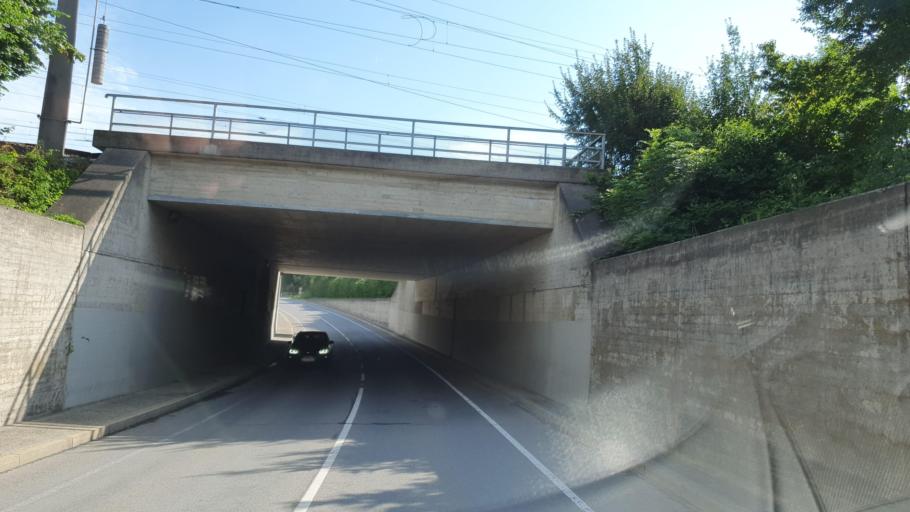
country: AT
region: Vorarlberg
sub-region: Politischer Bezirk Bregenz
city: Wolfurt
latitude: 47.4557
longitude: 9.7428
